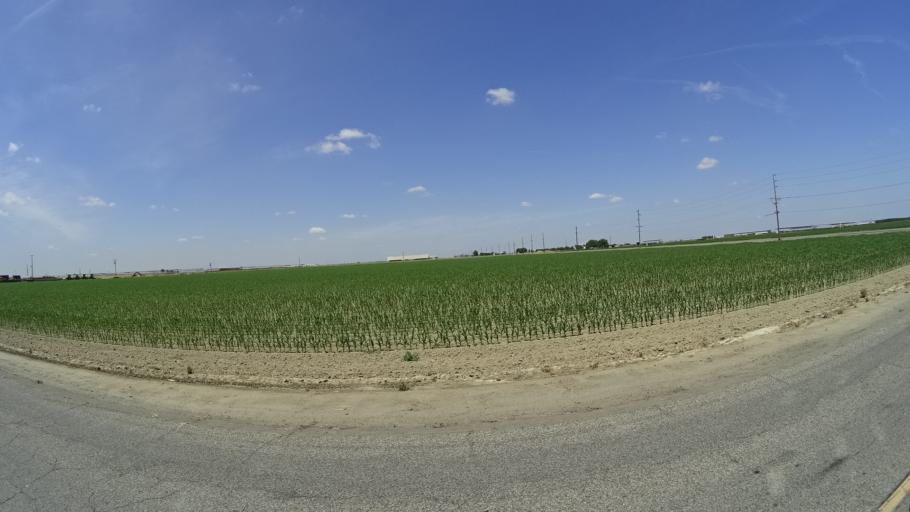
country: US
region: California
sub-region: Tulare County
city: Goshen
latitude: 36.2971
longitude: -119.4744
